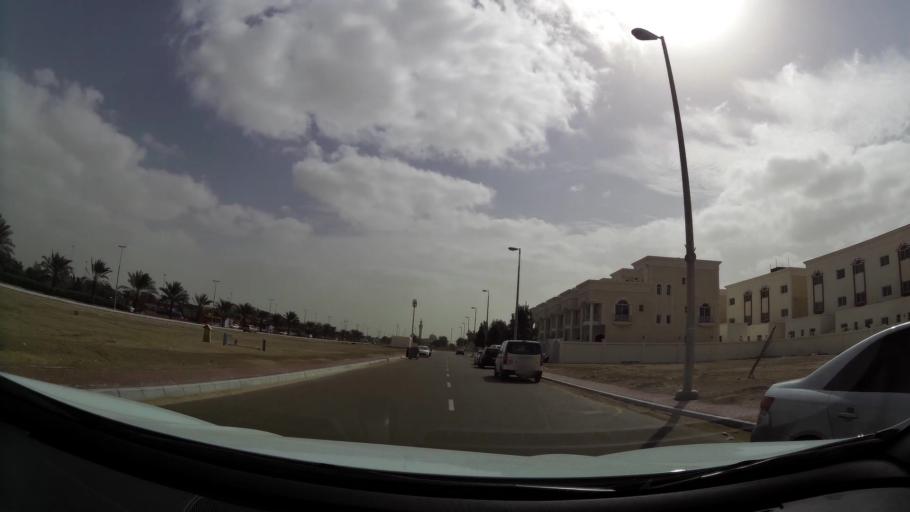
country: AE
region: Abu Dhabi
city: Abu Dhabi
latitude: 24.4120
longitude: 54.5037
